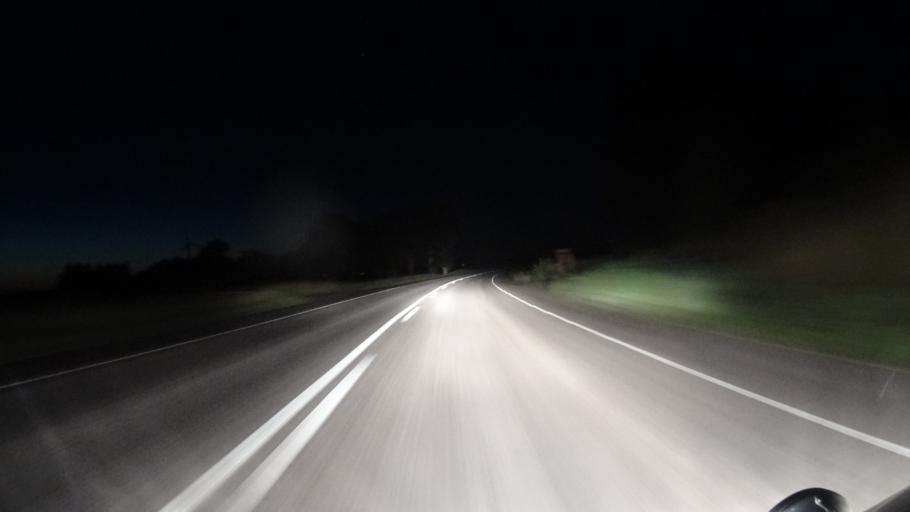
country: SE
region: OEstergoetland
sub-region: Vadstena Kommun
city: Herrestad
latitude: 58.2824
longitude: 14.7612
